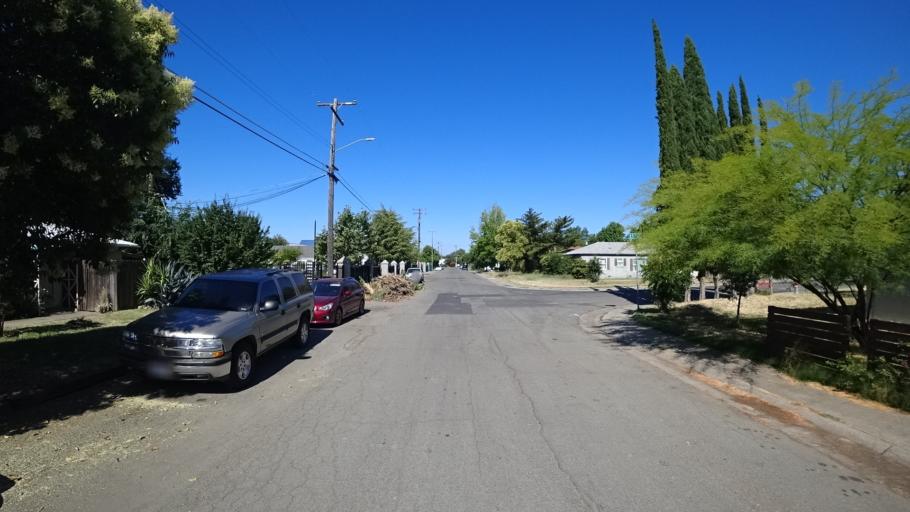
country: US
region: California
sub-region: Sacramento County
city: Parkway
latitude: 38.5266
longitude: -121.4809
